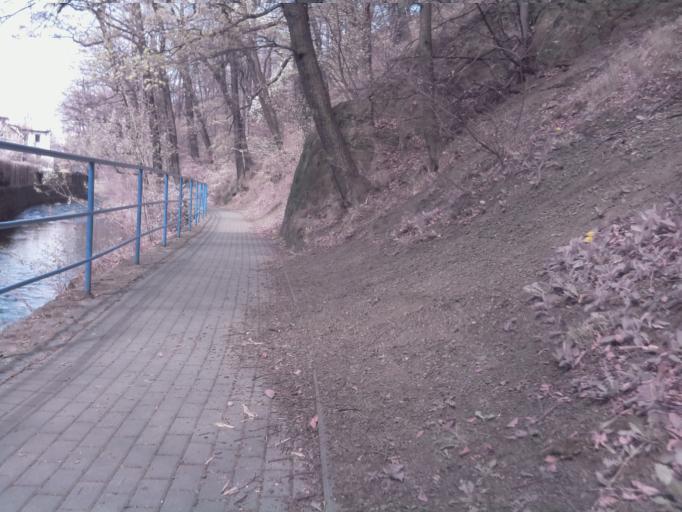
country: PL
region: Lower Silesian Voivodeship
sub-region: Powiat swidnicki
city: Swiebodzice
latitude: 50.8550
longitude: 16.3126
